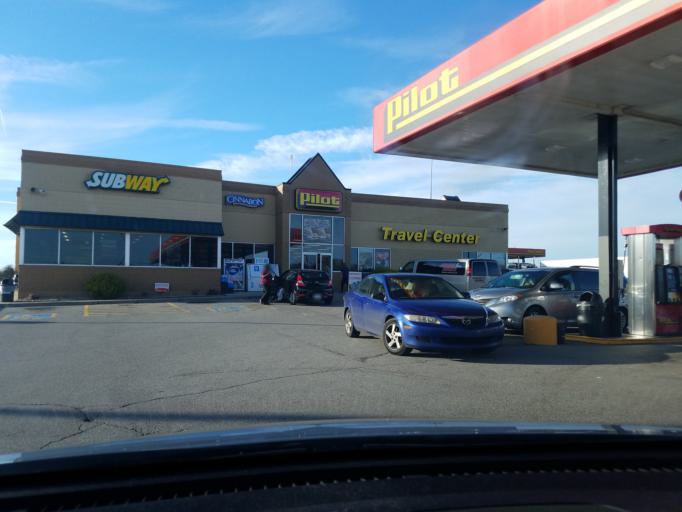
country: US
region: Indiana
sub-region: Crawford County
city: English
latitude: 38.2388
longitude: -86.3618
